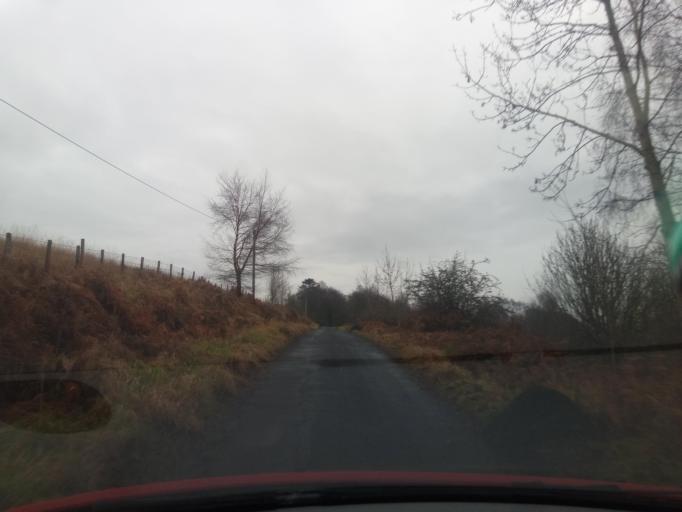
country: GB
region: England
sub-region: Northumberland
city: Rochester
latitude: 55.1776
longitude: -2.4301
